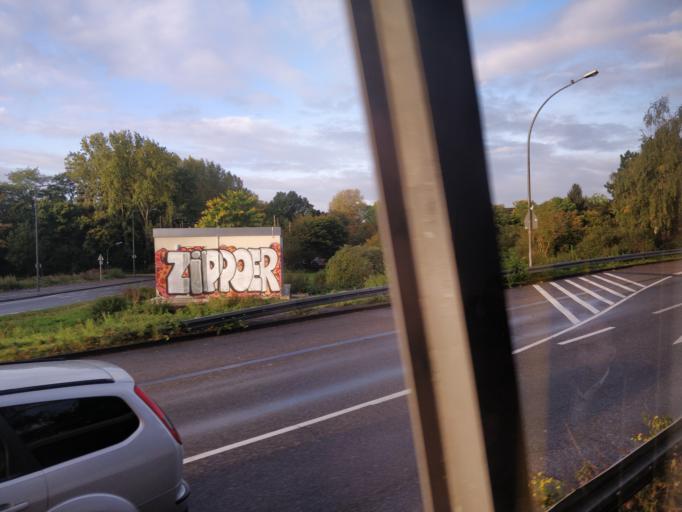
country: DE
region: North Rhine-Westphalia
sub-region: Regierungsbezirk Koln
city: Riehl
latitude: 50.9661
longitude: 6.9892
